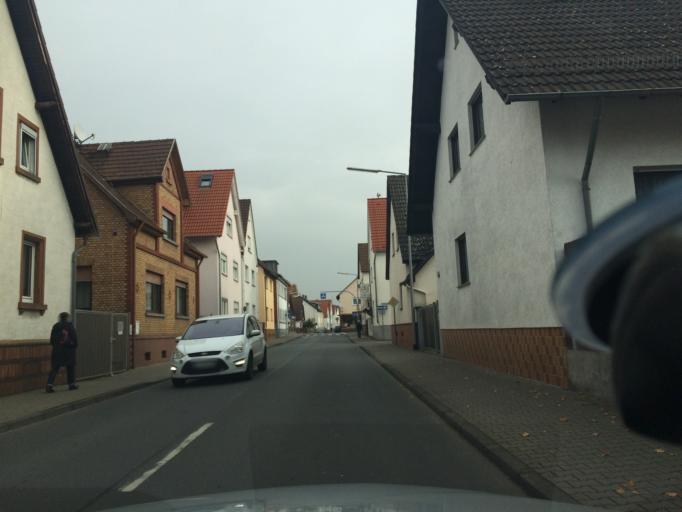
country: DE
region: Hesse
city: Morfelden-Walldorf
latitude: 49.9776
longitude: 8.5650
